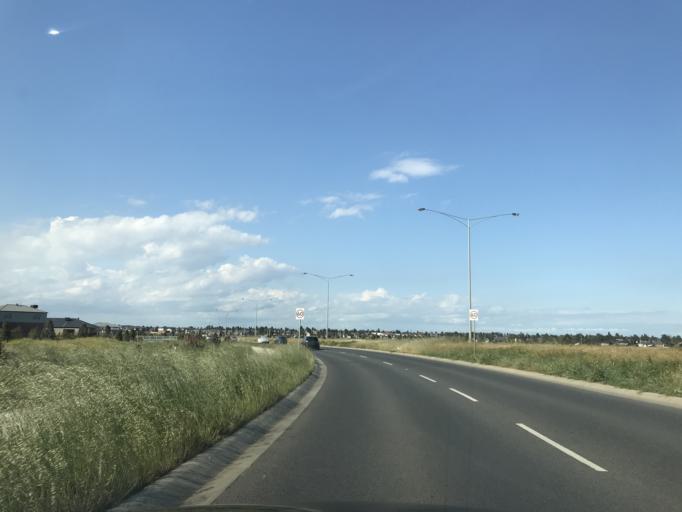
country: AU
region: Victoria
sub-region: Wyndham
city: Hoppers Crossing
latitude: -37.8982
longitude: 144.7110
